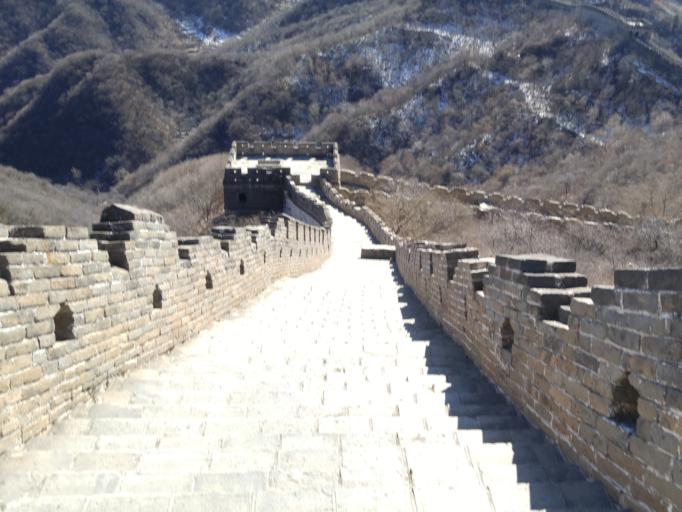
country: CN
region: Beijing
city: Bohai
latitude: 40.4477
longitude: 116.5545
